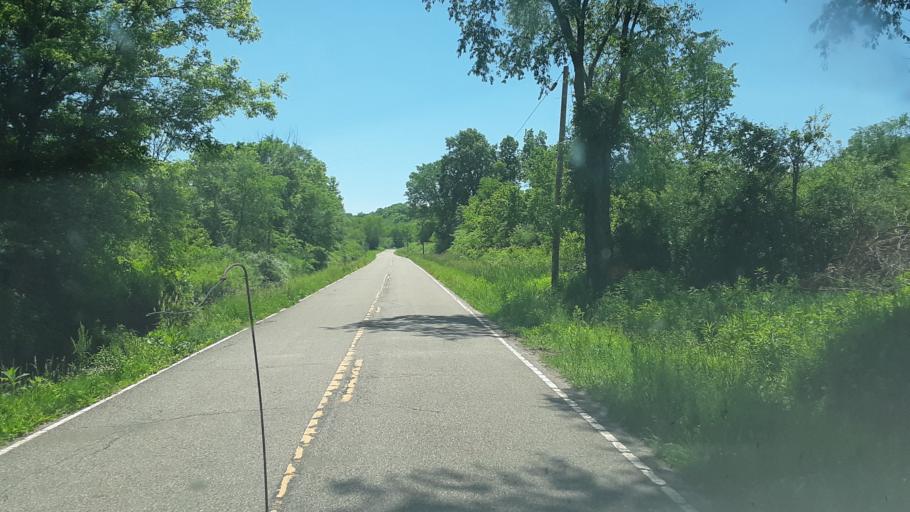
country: US
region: Ohio
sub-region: Coshocton County
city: Coshocton
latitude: 40.2966
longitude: -82.0071
